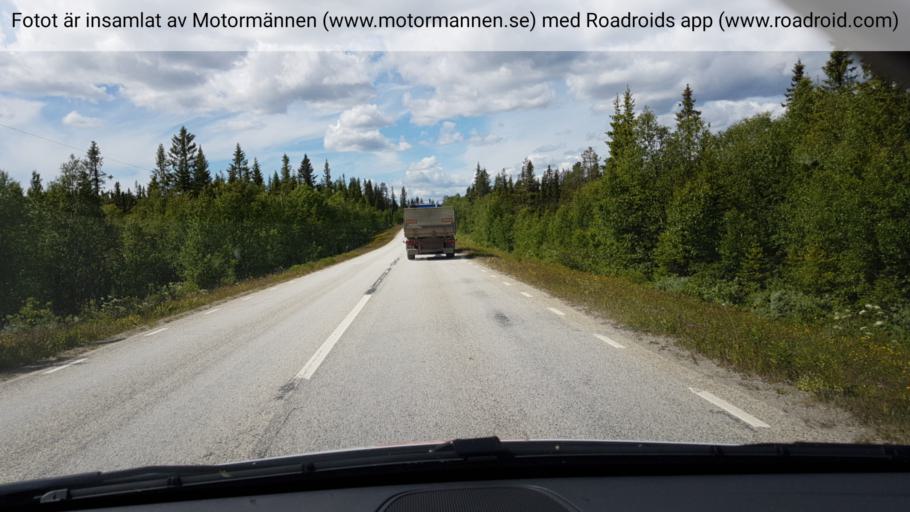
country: SE
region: Jaemtland
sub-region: Bergs Kommun
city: Hoverberg
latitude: 62.5402
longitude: 14.2478
